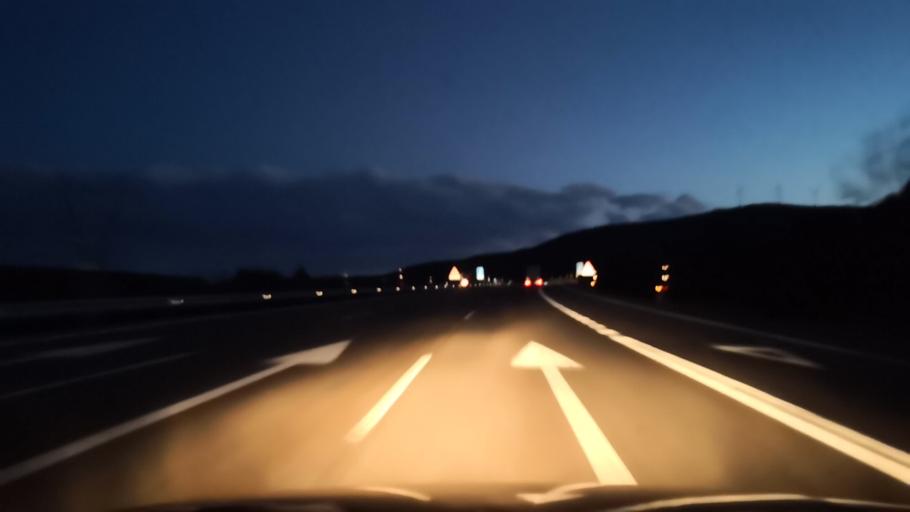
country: ES
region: Castille and Leon
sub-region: Provincia de Leon
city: Villagaton
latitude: 42.5781
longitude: -6.2158
